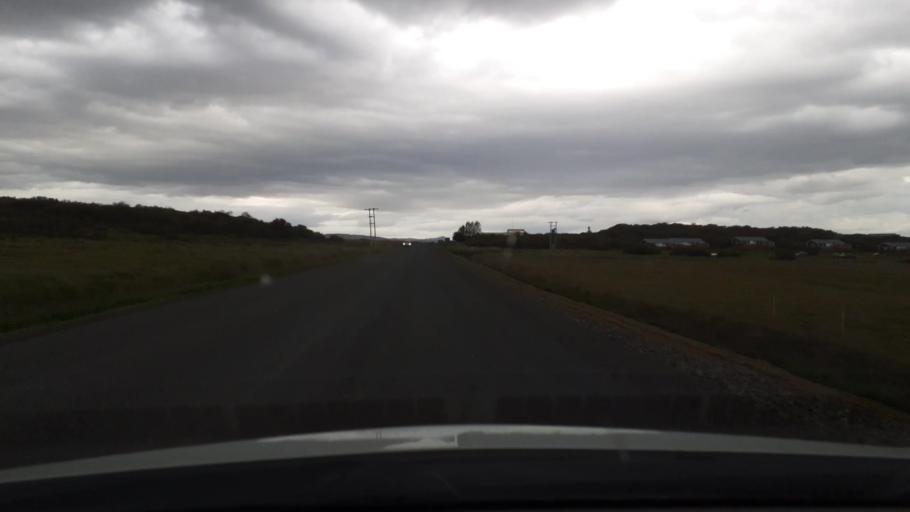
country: IS
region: West
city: Borgarnes
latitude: 64.6717
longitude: -21.7013
